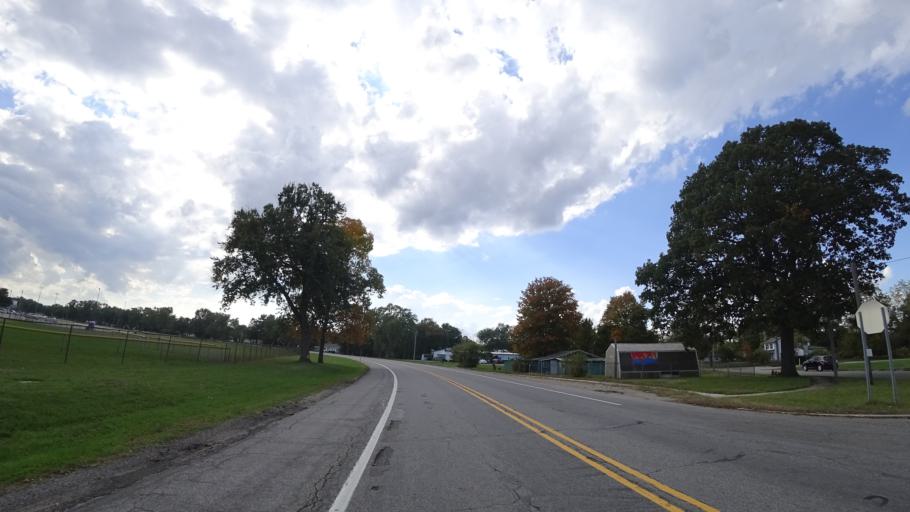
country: US
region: Michigan
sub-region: Saint Joseph County
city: Three Rivers
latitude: 41.9545
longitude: -85.6177
